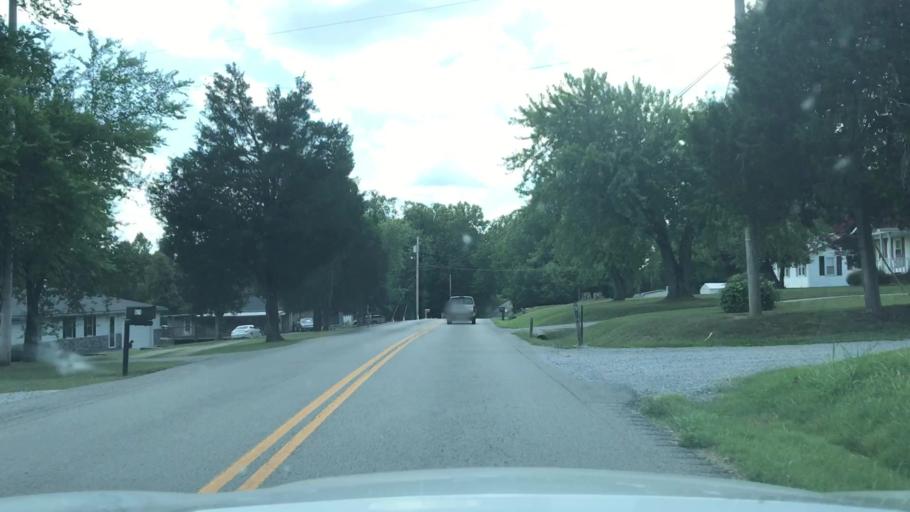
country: US
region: Kentucky
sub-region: Muhlenberg County
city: Greenville
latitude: 37.1909
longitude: -87.2180
